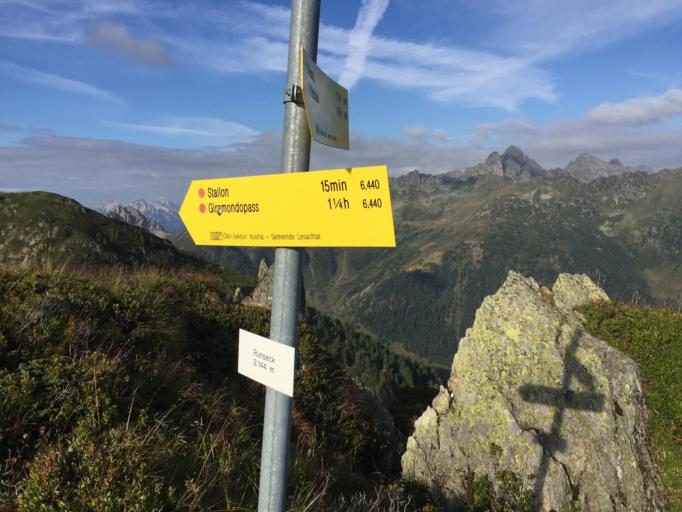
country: IT
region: Friuli Venezia Giulia
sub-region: Provincia di Udine
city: Rigolato
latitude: 46.6512
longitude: 12.8489
